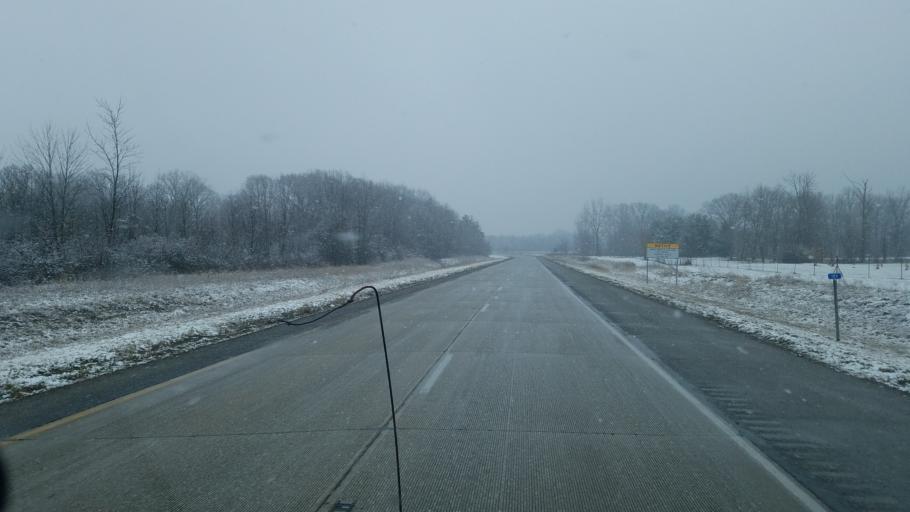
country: US
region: Indiana
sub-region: Grant County
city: Marion
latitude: 40.5545
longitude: -85.6423
